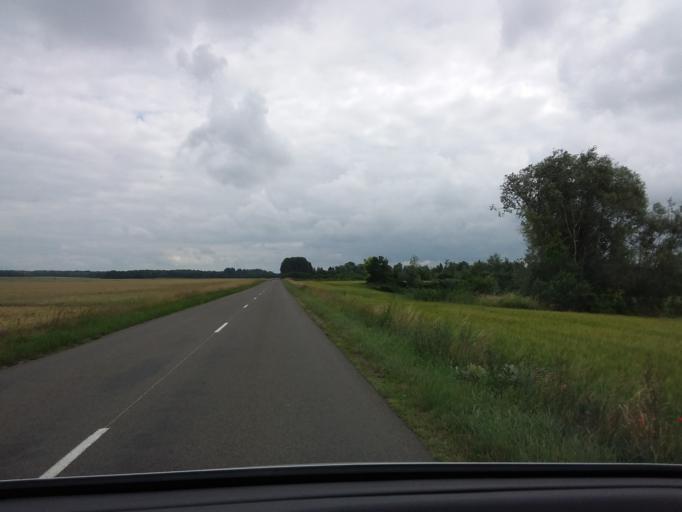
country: FR
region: Champagne-Ardenne
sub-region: Departement de la Marne
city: Cormicy
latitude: 49.4086
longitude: 3.8308
